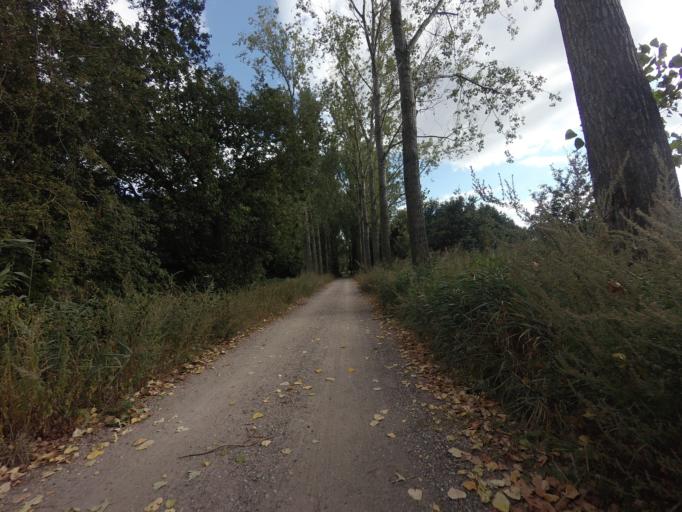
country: NL
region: North Brabant
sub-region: Gemeente Grave
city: Grave
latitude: 51.7357
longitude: 5.7412
